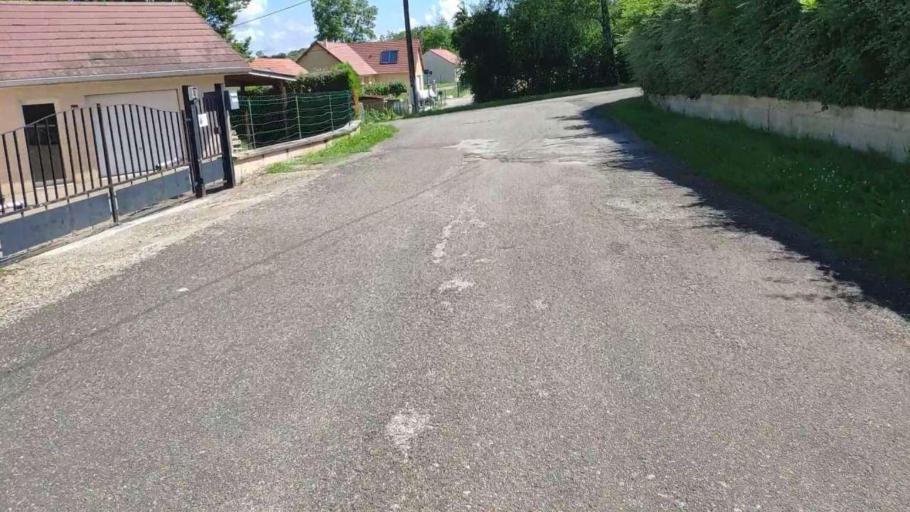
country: FR
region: Franche-Comte
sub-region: Departement du Jura
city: Bletterans
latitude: 46.8245
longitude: 5.5555
